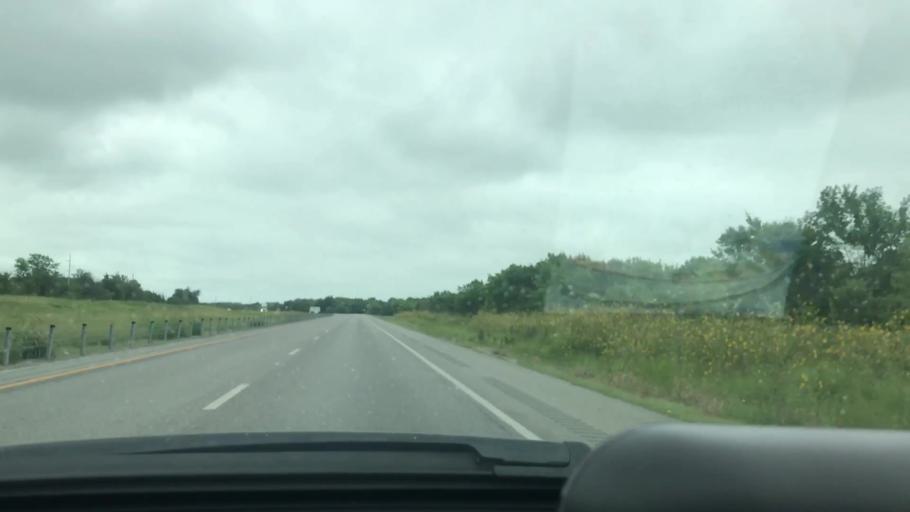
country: US
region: Oklahoma
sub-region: Coal County
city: Coalgate
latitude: 34.6445
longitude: -95.9463
